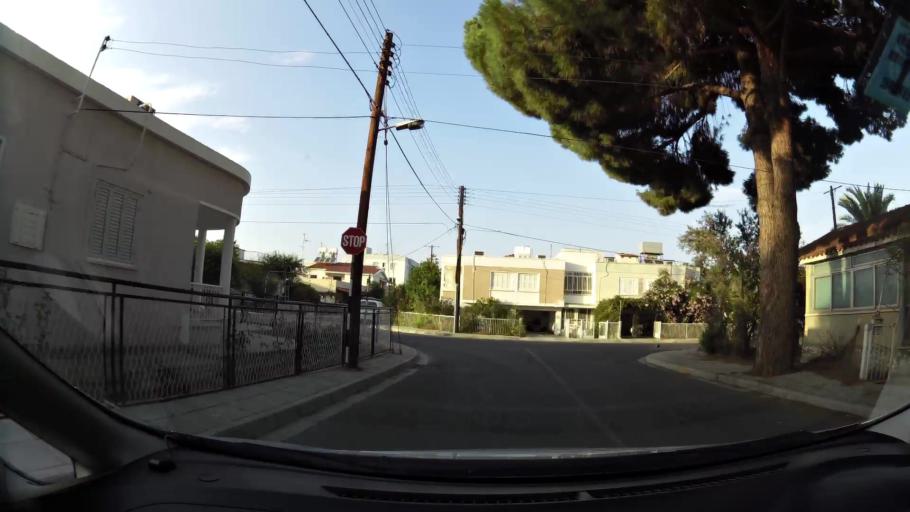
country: CY
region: Lefkosia
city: Nicosia
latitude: 35.1704
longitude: 33.3268
